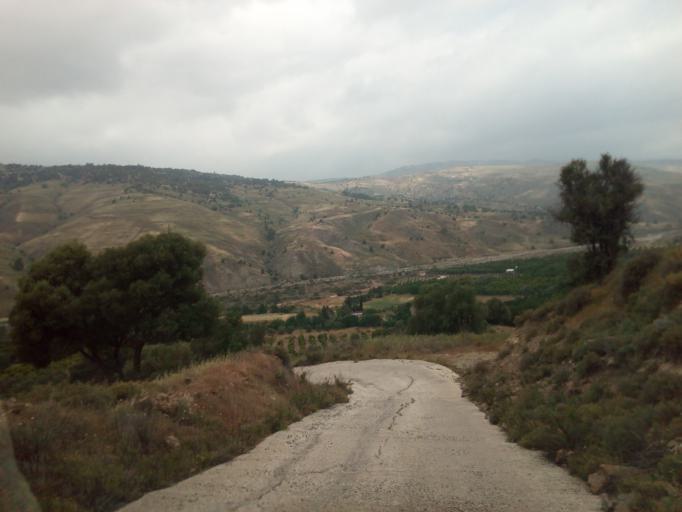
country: CY
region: Limassol
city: Pissouri
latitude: 34.8146
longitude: 32.6295
